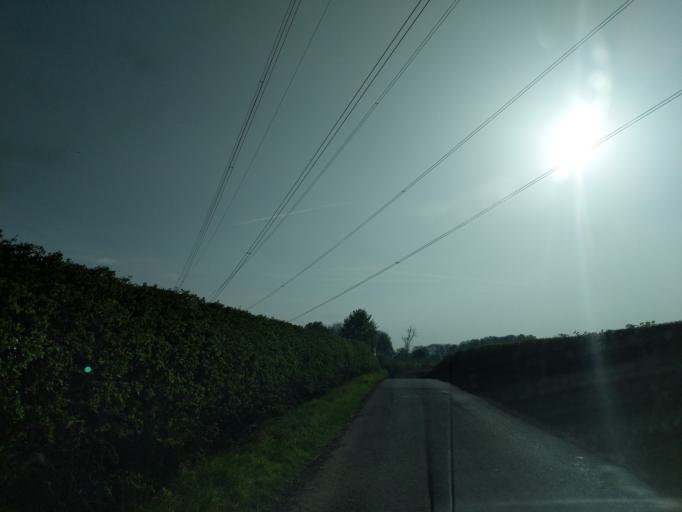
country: GB
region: Scotland
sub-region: Fife
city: Pathhead
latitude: 55.8563
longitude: -2.9388
